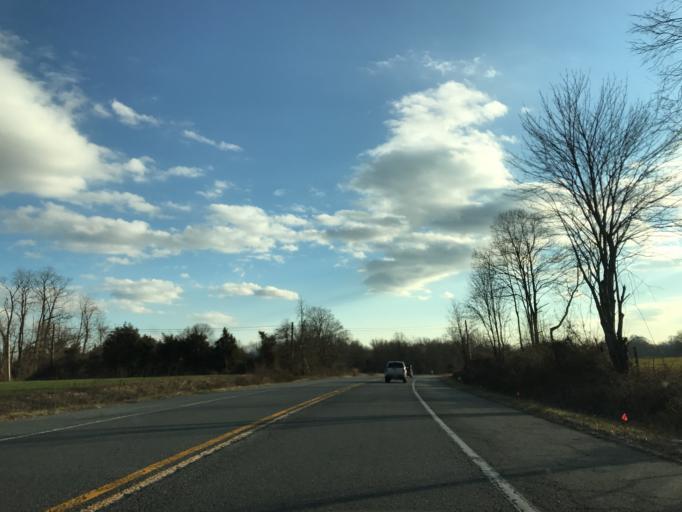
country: US
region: Maryland
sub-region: Cecil County
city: North East
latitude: 39.6538
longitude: -75.9527
